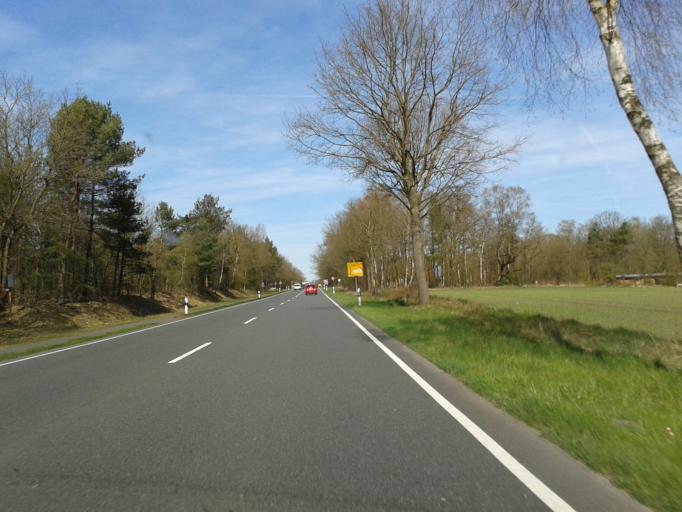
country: DE
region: Lower Saxony
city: Munster
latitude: 52.9718
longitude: 10.1064
